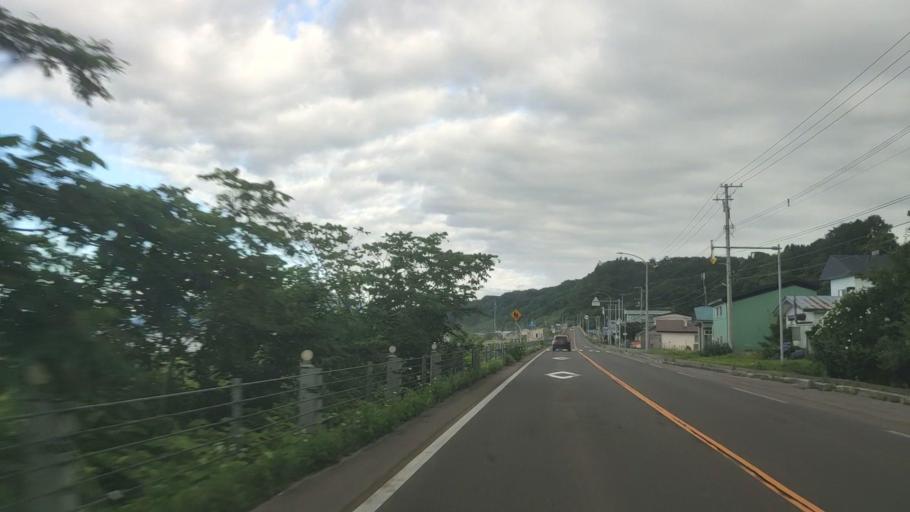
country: JP
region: Hokkaido
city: Nanae
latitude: 42.1316
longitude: 140.5112
